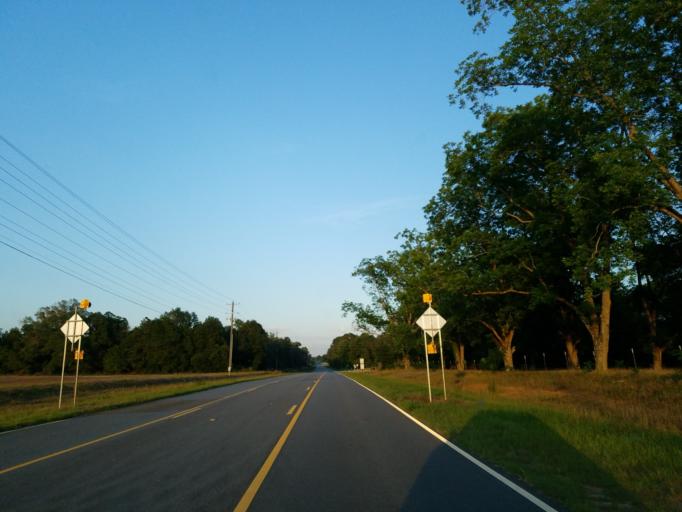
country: US
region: Georgia
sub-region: Crisp County
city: Cordele
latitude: 31.9262
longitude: -83.7585
